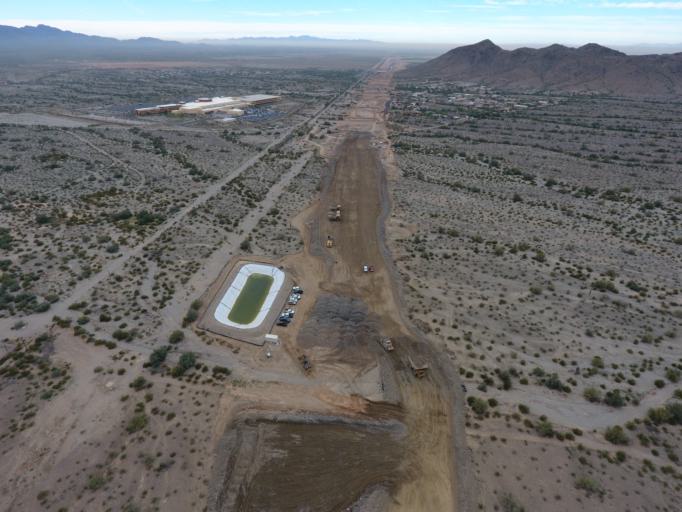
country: US
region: Arizona
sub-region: Maricopa County
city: Laveen
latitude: 33.3058
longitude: -112.1467
